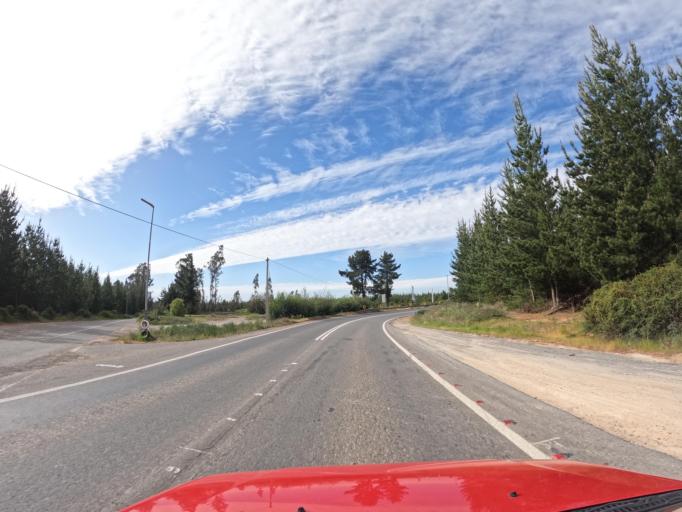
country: CL
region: O'Higgins
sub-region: Provincia de Colchagua
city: Santa Cruz
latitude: -34.3085
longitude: -71.8508
